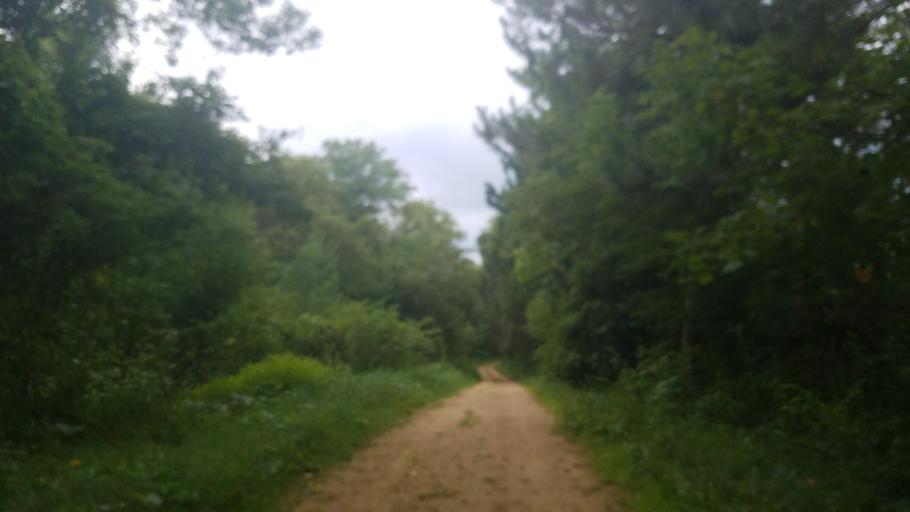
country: US
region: Wisconsin
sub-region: Dunn County
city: Menomonie
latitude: 44.7748
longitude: -91.9369
